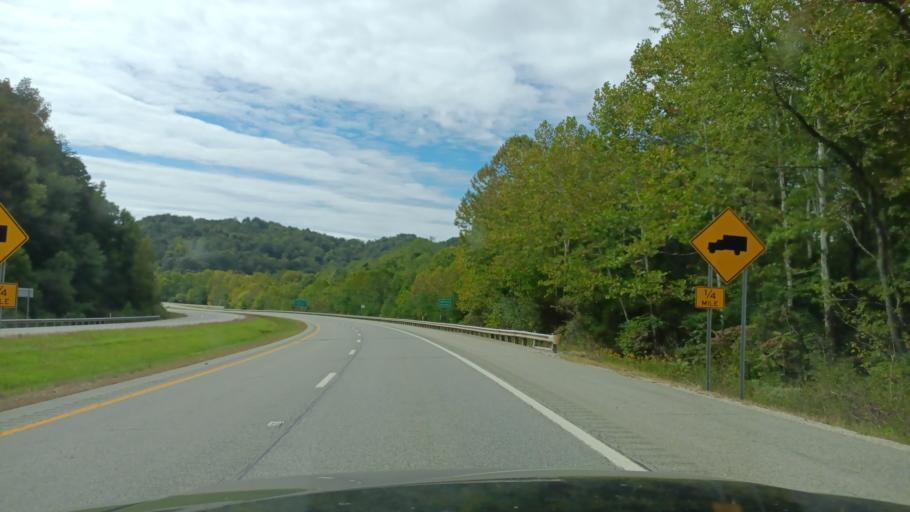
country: US
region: West Virginia
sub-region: Ritchie County
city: Pennsboro
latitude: 39.2702
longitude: -80.9112
